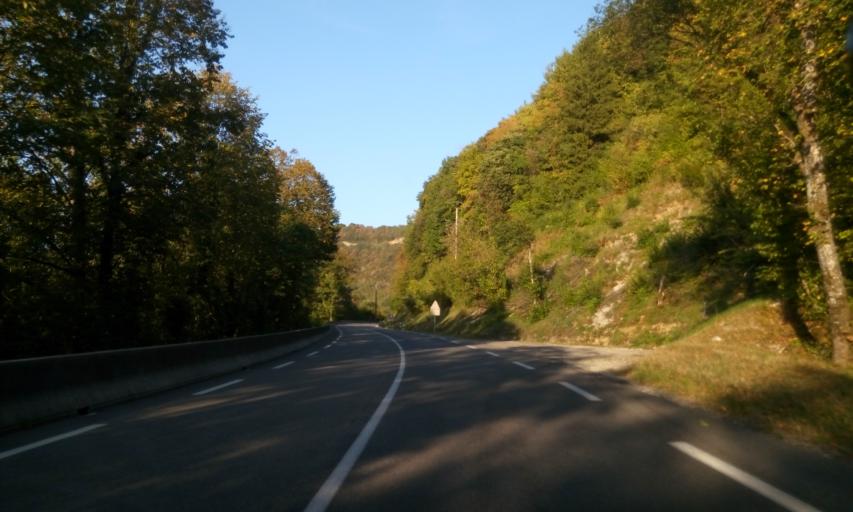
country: FR
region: Rhone-Alpes
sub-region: Departement de l'Ain
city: Poncin
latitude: 46.0785
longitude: 5.4630
